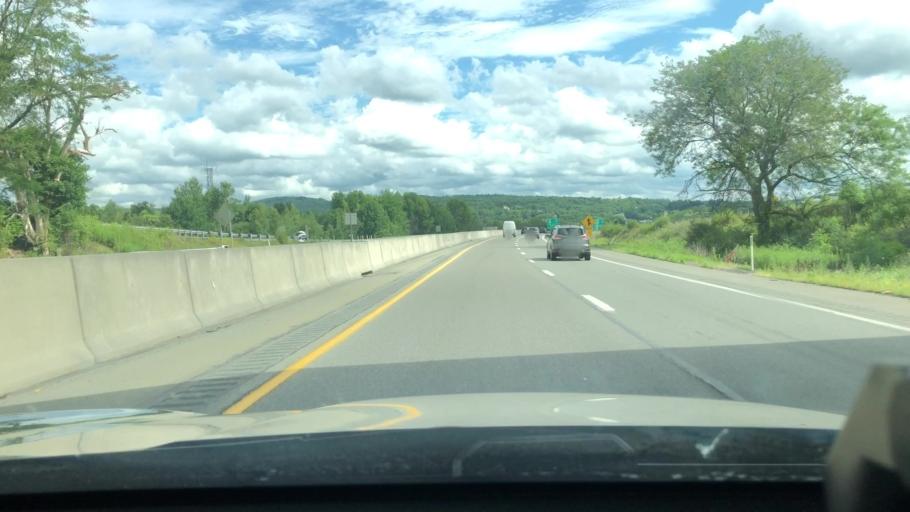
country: US
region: Pennsylvania
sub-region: Monroe County
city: Saylorsburg
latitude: 40.9482
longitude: -75.2915
